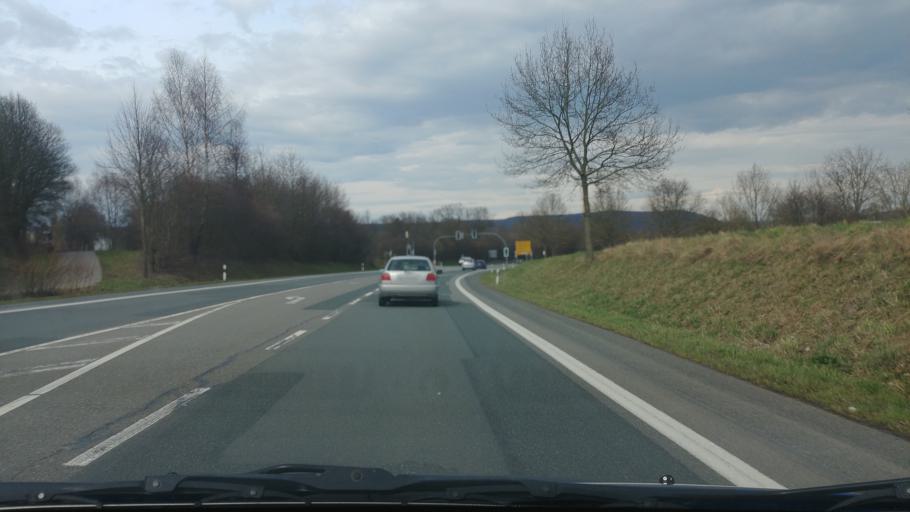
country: DE
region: North Rhine-Westphalia
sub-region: Regierungsbezirk Detmold
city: Hoexter
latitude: 51.8139
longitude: 9.4018
